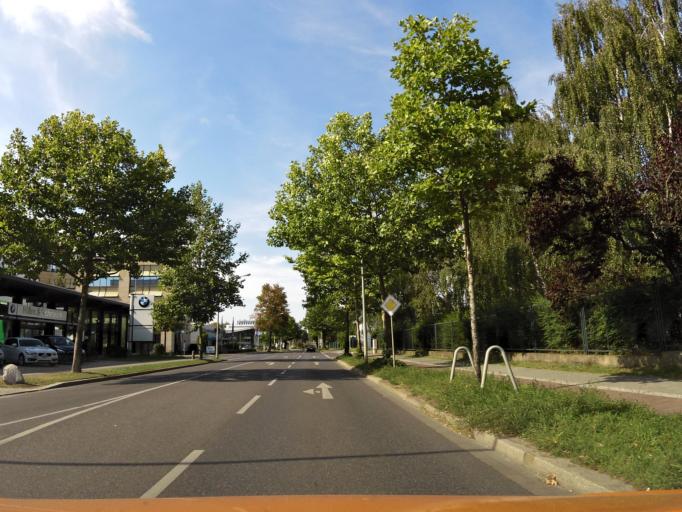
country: DE
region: Brandenburg
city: Teltow
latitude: 52.3976
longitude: 13.2431
